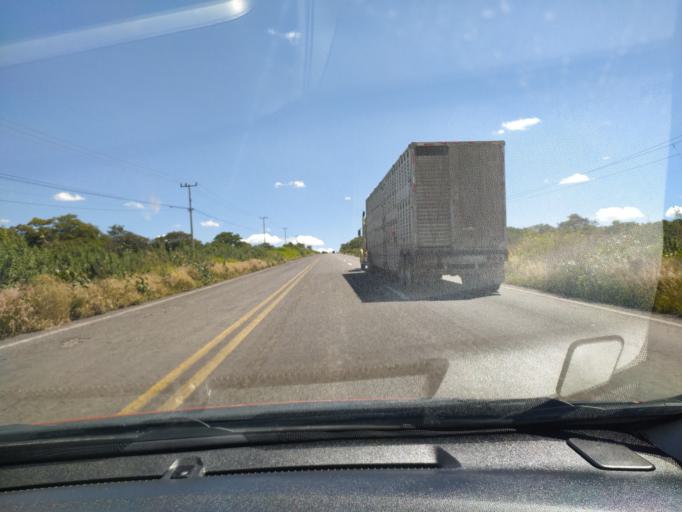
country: MX
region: Jalisco
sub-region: San Julian
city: Colonia Veintitres de Mayo
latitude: 21.0090
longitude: -102.2638
